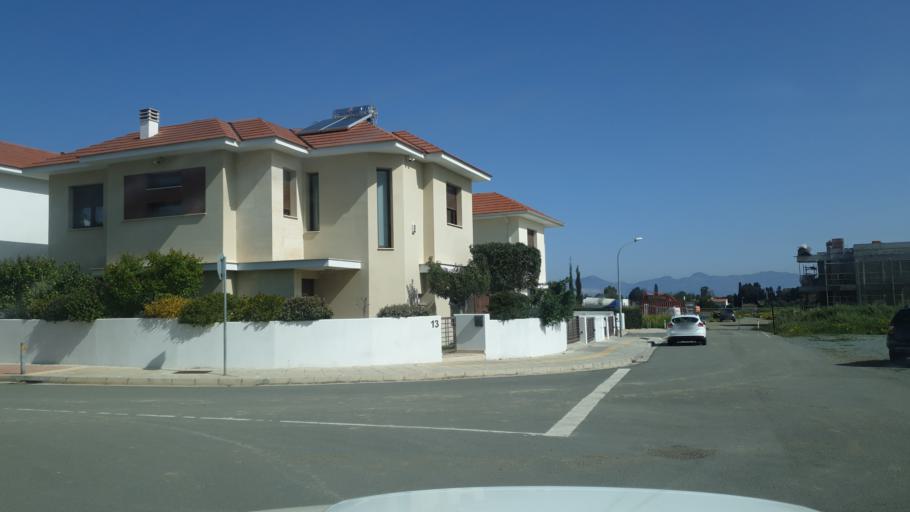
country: CY
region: Lefkosia
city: Tseri
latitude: 35.1306
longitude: 33.3215
